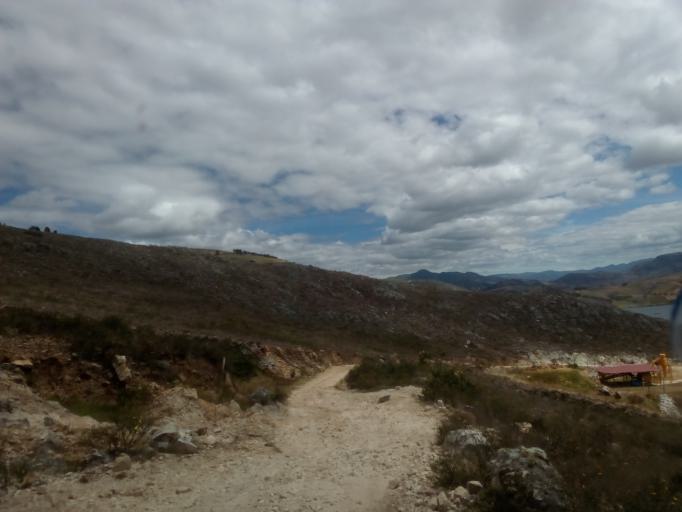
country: PE
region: La Libertad
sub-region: Sanchez Carrion
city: Curgos
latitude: -7.8001
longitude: -77.9742
